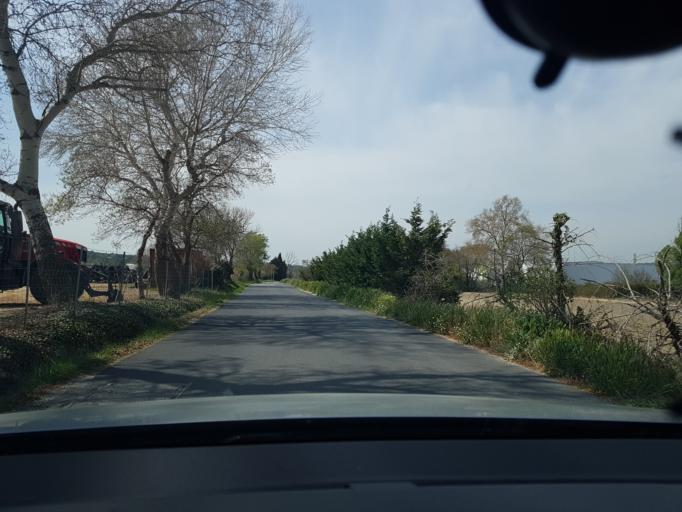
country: FR
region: Provence-Alpes-Cote d'Azur
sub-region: Departement des Bouches-du-Rhone
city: Bouc-Bel-Air
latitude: 43.4763
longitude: 5.3877
